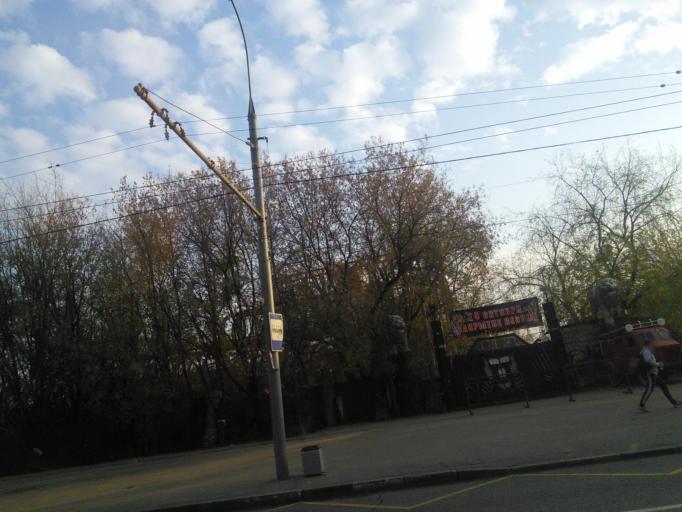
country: RU
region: Moskovskaya
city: Khoroshevo-Mnevniki
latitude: 55.7658
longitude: 37.4717
